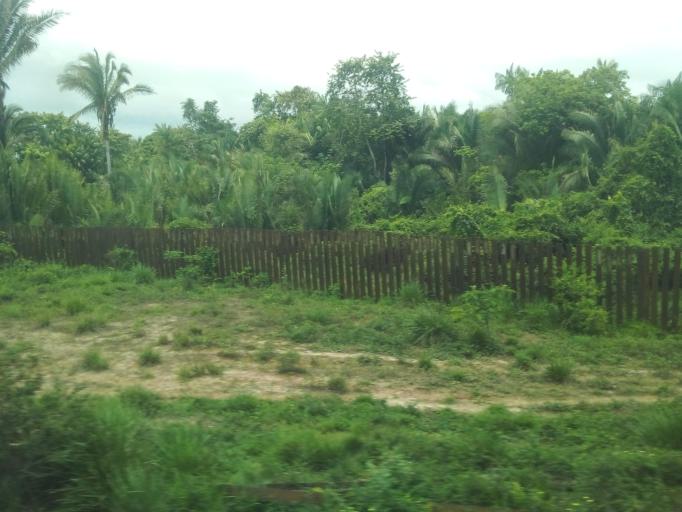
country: BR
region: Maranhao
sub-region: Vitoria Do Mearim
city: Vitoria do Mearim
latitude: -3.5913
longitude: -44.9783
